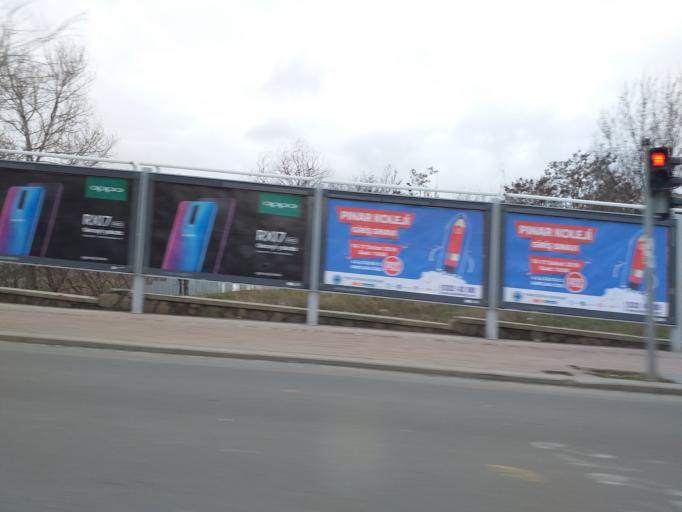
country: TR
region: Ankara
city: Ankara
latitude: 39.9672
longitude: 32.8383
